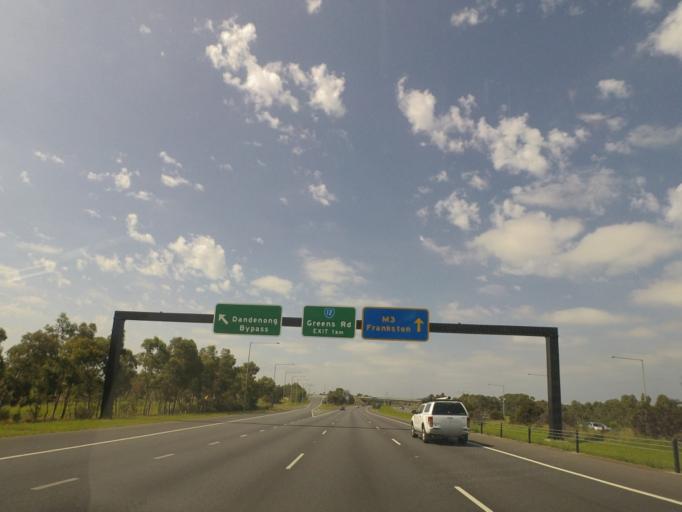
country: AU
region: Victoria
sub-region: Greater Dandenong
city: Dandenong
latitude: -37.9969
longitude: 145.1918
